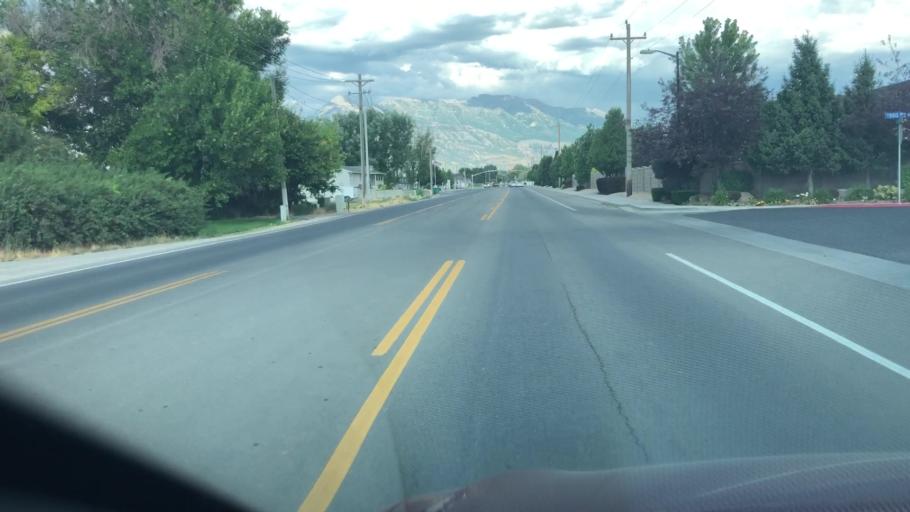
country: US
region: Utah
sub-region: Utah County
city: Lehi
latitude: 40.3872
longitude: -111.8808
